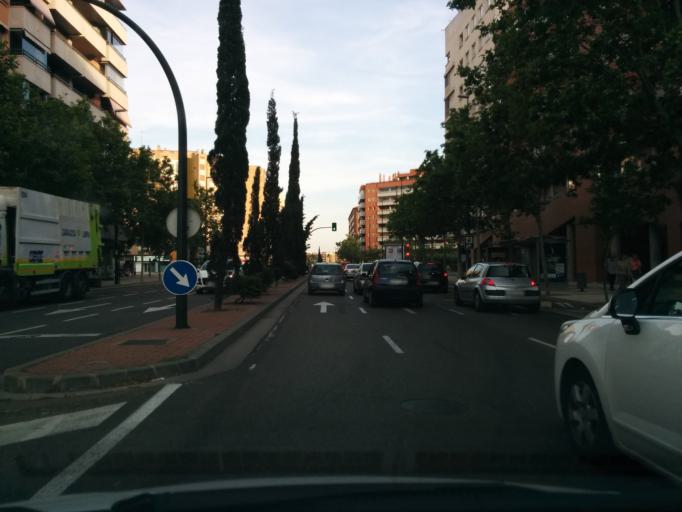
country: ES
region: Aragon
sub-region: Provincia de Zaragoza
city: Zaragoza
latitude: 41.6632
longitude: -0.8659
